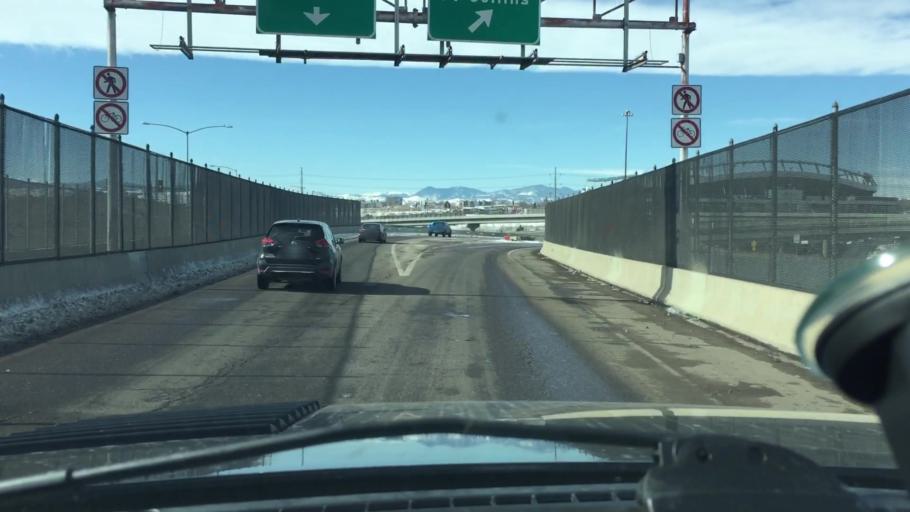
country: US
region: Colorado
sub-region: Denver County
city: Denver
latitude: 39.7406
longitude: -105.0115
